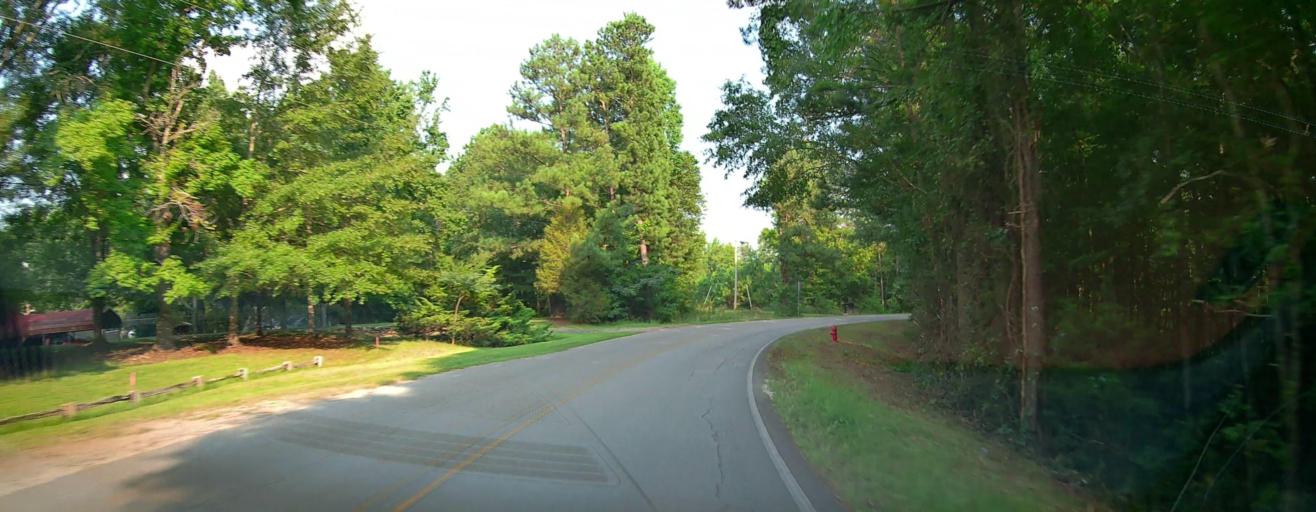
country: US
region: Georgia
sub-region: Monroe County
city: Forsyth
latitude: 32.9986
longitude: -83.7674
